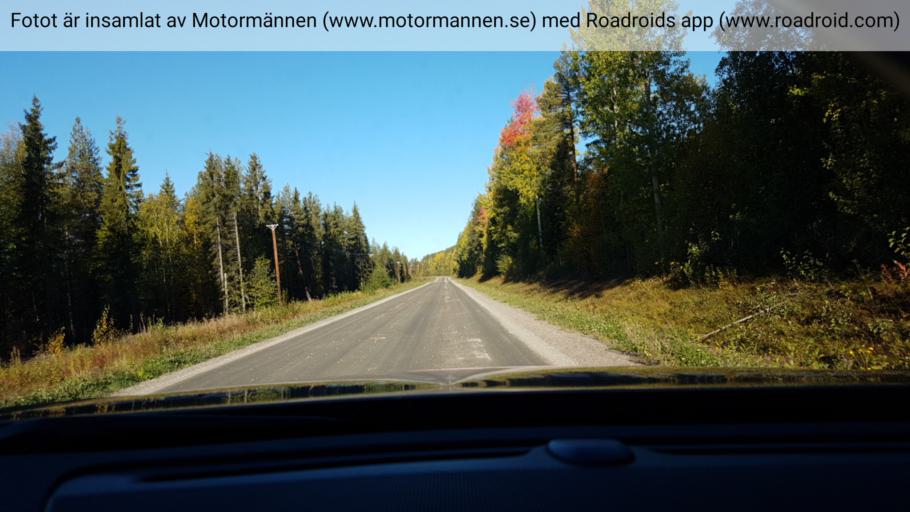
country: SE
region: Norrbotten
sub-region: Alvsbyns Kommun
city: AElvsbyn
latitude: 66.1776
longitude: 21.2360
